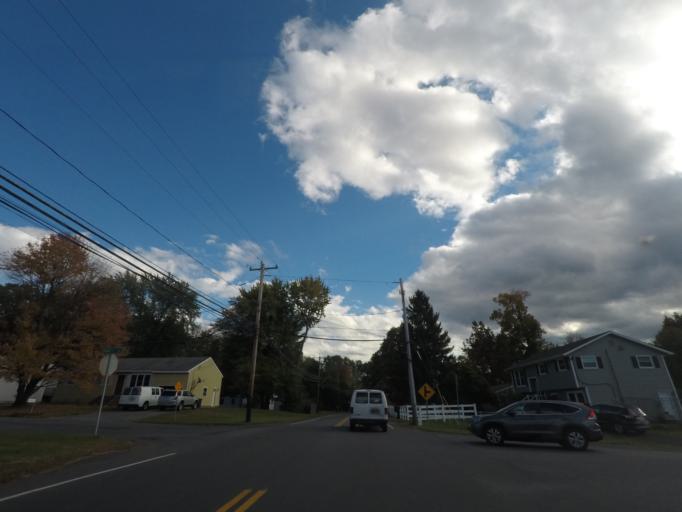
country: US
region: New York
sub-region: Schenectady County
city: Niskayuna
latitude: 42.7496
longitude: -73.8383
